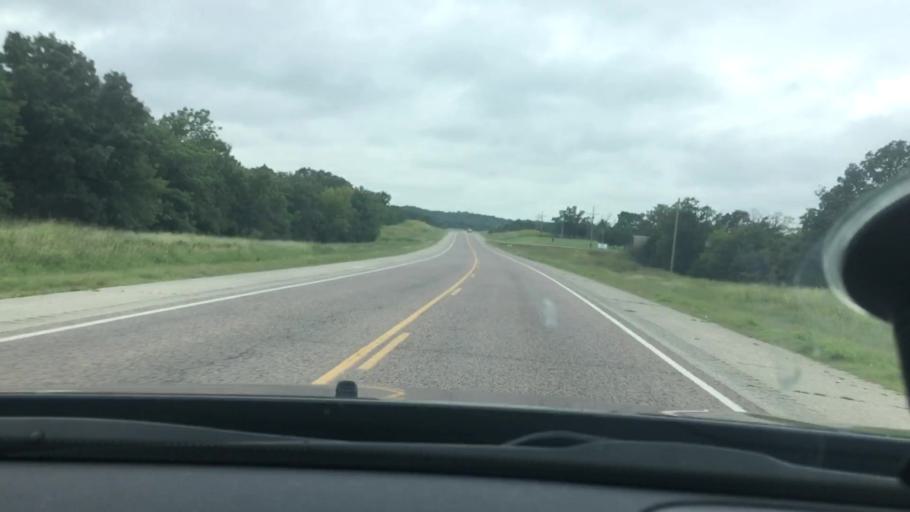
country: US
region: Oklahoma
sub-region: Pontotoc County
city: Ada
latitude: 34.7959
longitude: -96.5527
